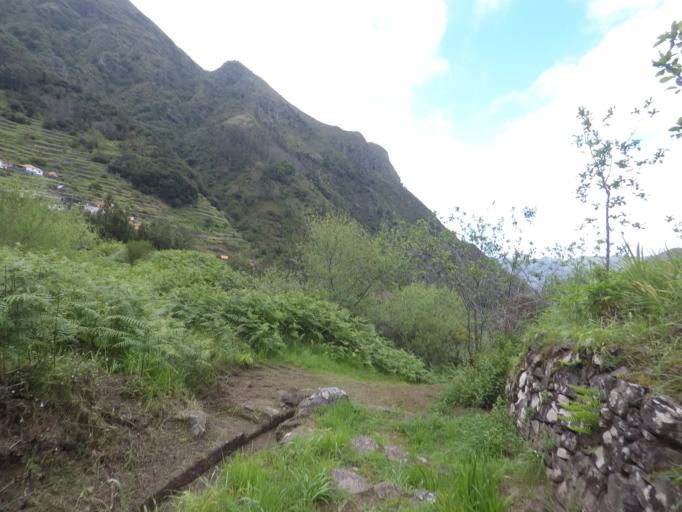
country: PT
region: Madeira
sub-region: Camara de Lobos
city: Curral das Freiras
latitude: 32.7796
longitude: -16.9805
